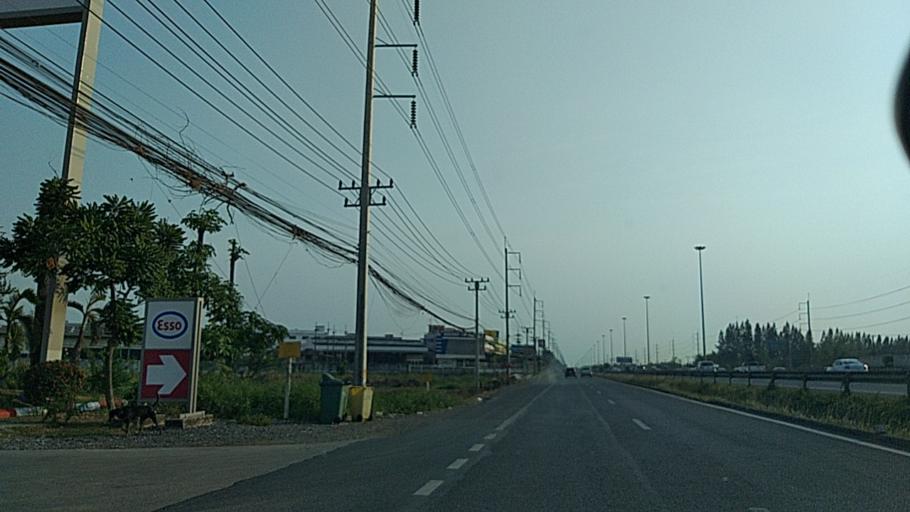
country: TH
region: Sara Buri
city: Nong Khae
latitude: 14.3155
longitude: 100.8372
